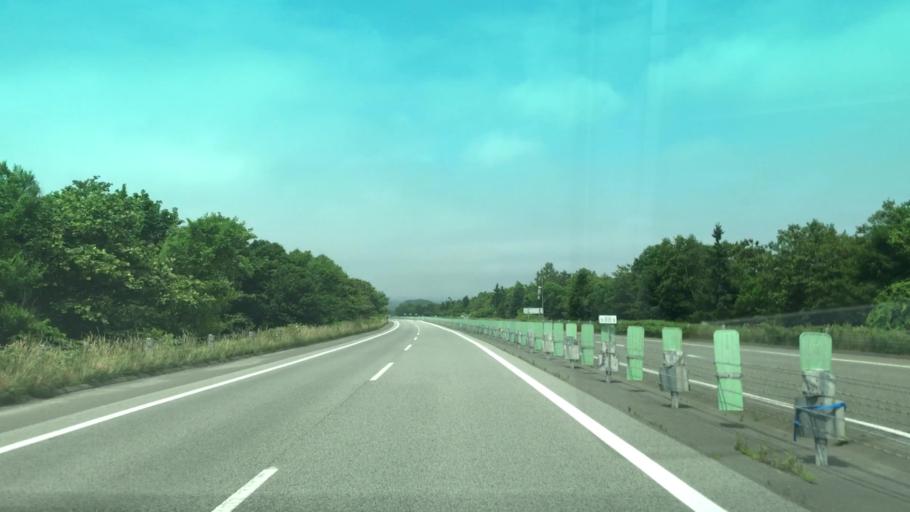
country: JP
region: Hokkaido
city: Shiraoi
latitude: 42.5121
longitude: 141.2698
